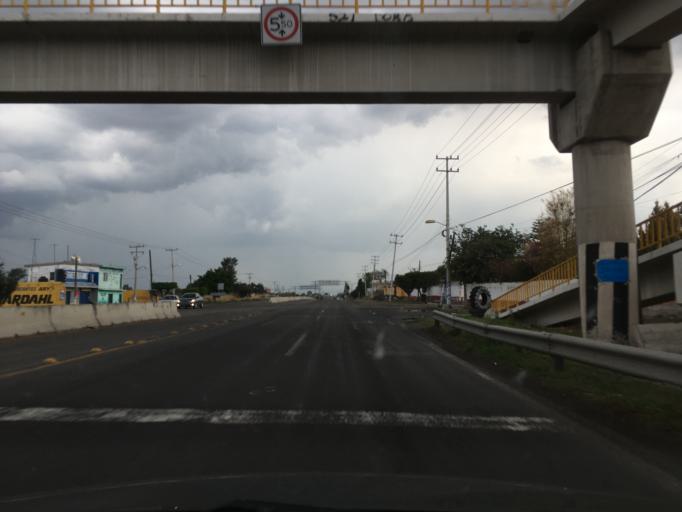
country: MX
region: Guanajuato
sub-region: Celaya
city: El Sauz (El Sauz de Villasenor)
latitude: 20.3877
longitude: -100.7920
